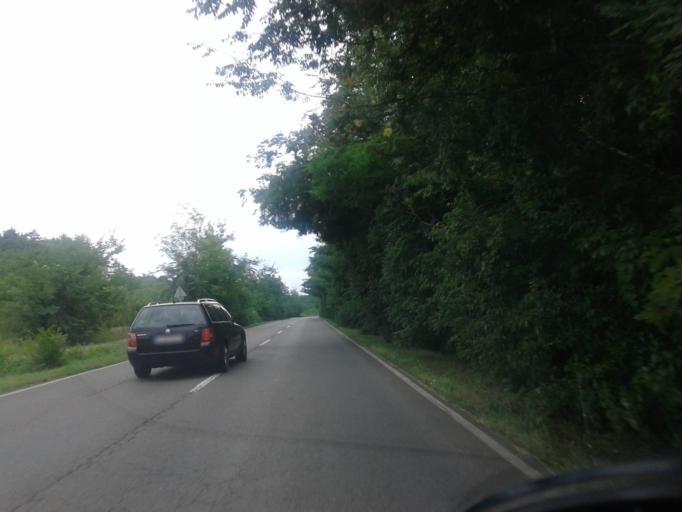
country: HU
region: Csongrad
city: Asotthalom
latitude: 46.2180
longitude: 19.8046
